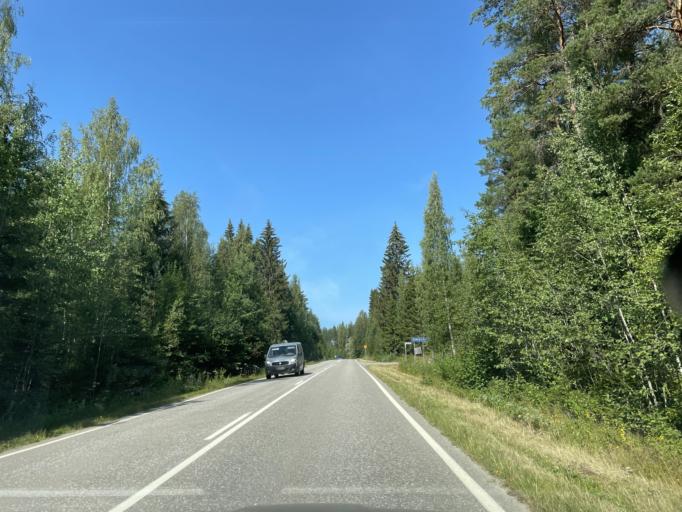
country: FI
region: Central Finland
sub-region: Saarijaervi-Viitasaari
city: Pihtipudas
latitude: 63.3624
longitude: 25.7434
